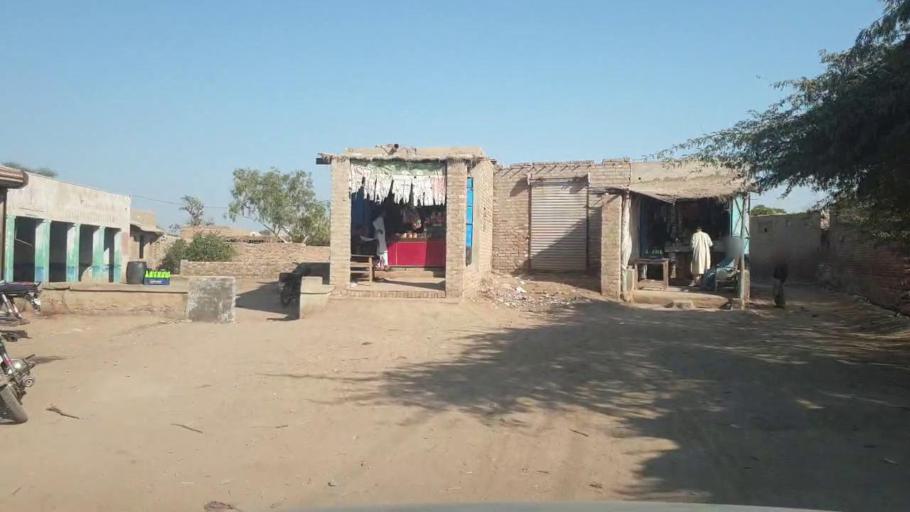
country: PK
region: Sindh
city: Chambar
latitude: 25.2872
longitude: 68.8538
